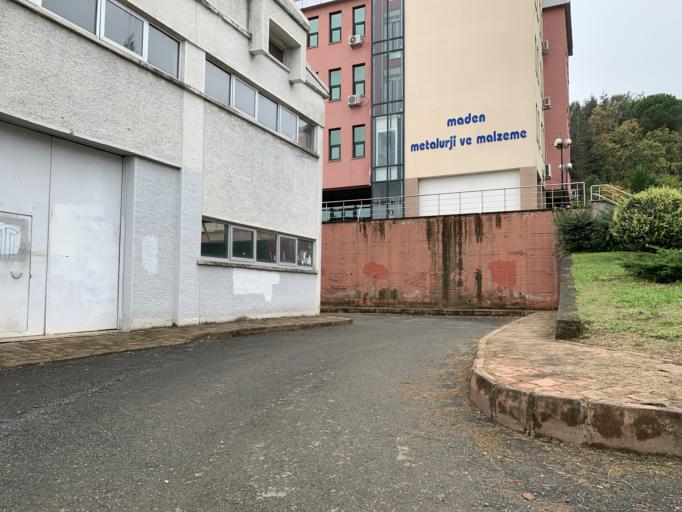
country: TR
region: Trabzon
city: Trabzon
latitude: 40.9941
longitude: 39.7737
